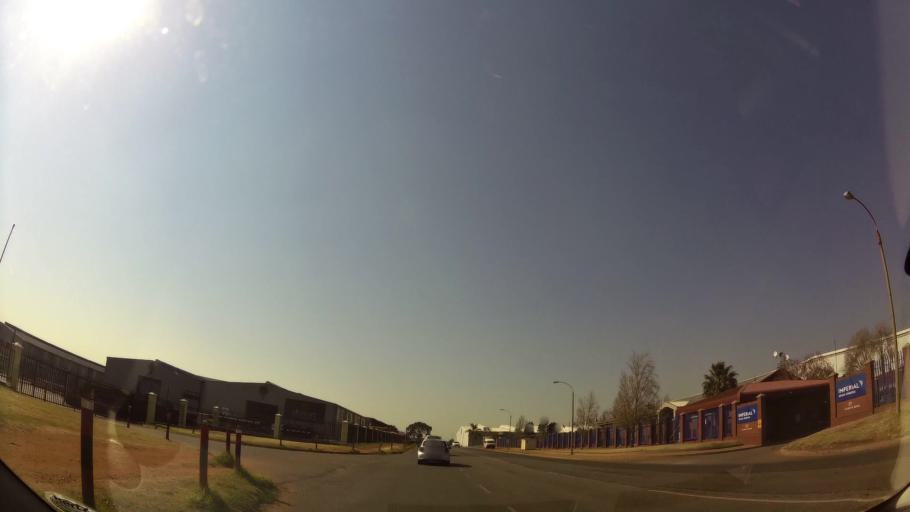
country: ZA
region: Gauteng
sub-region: Ekurhuleni Metropolitan Municipality
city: Boksburg
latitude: -26.1710
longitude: 28.2217
